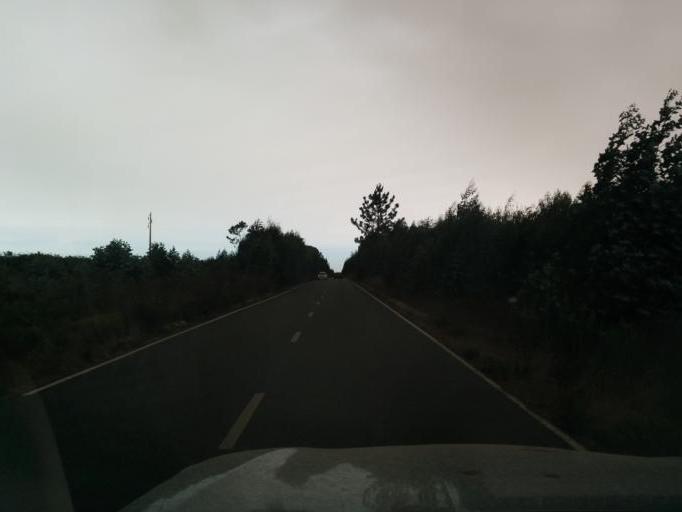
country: PT
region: Beja
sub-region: Odemira
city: Sao Teotonio
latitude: 37.5781
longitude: -8.7381
